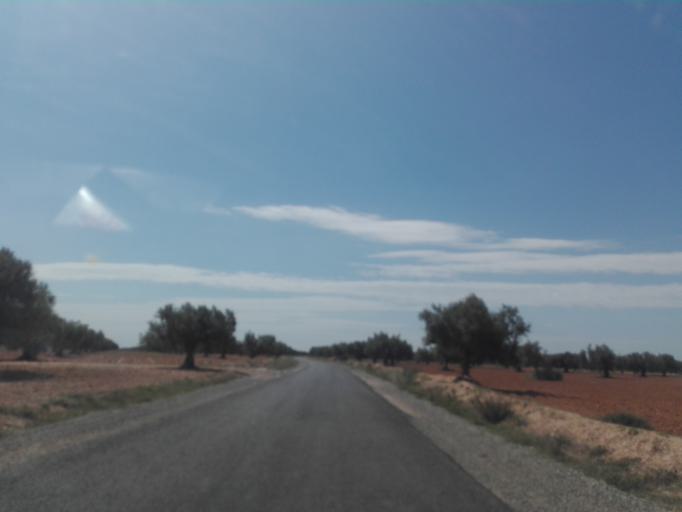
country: TN
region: Safaqis
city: Sfax
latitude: 34.6772
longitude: 10.5705
